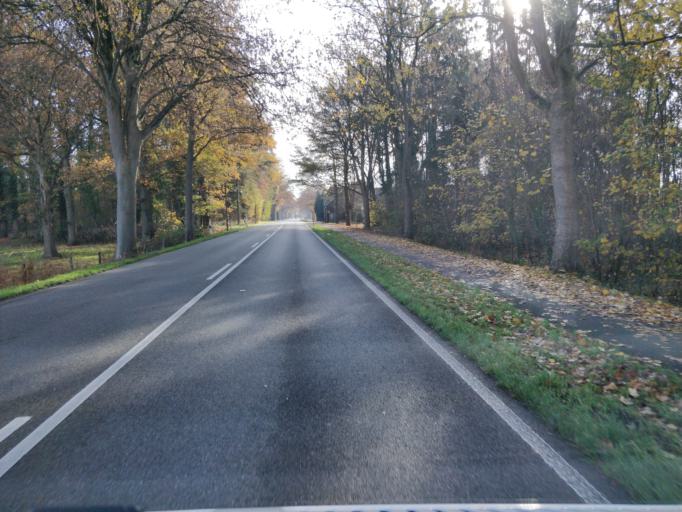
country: DE
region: North Rhine-Westphalia
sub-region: Regierungsbezirk Dusseldorf
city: Mehrhoog
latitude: 51.7236
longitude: 6.5103
